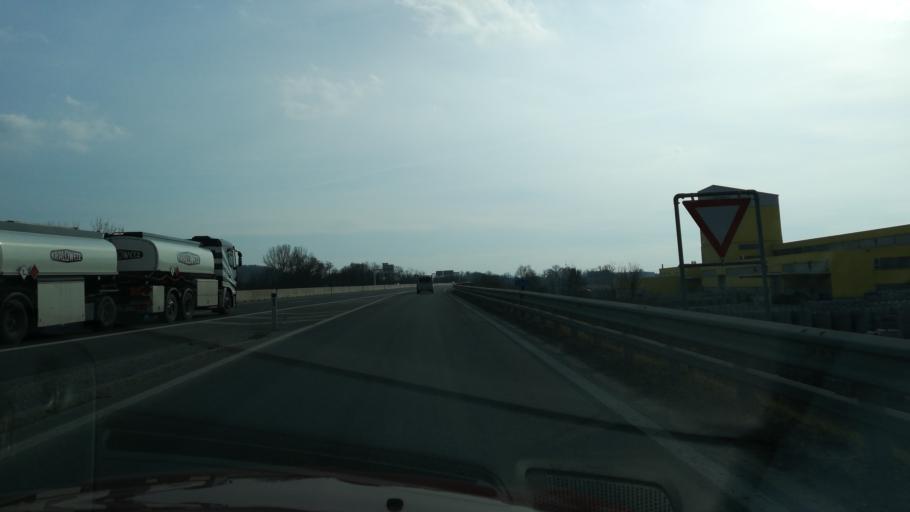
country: AT
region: Lower Austria
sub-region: Politischer Bezirk Sankt Polten
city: Traismauer
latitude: 48.3416
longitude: 15.7233
